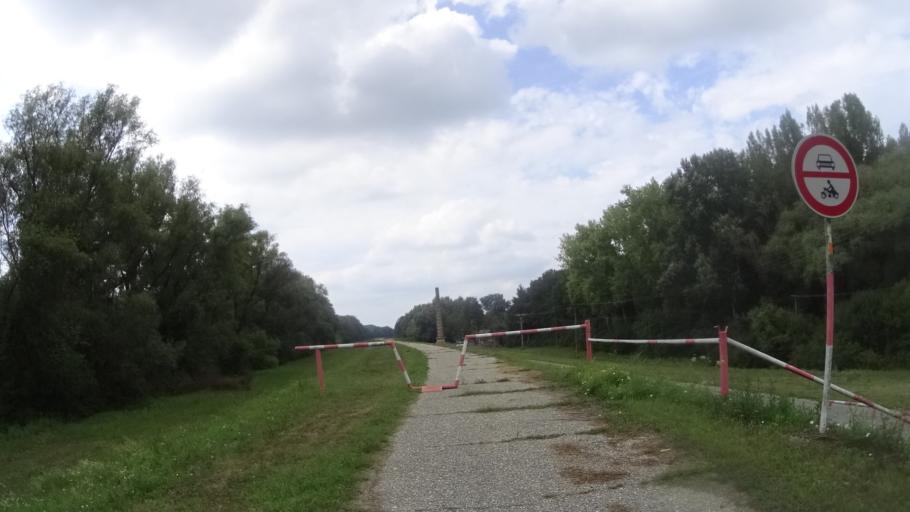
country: SK
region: Trnavsky
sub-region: Okres Dunajska Streda
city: Velky Meder
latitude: 47.7637
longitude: 17.7314
